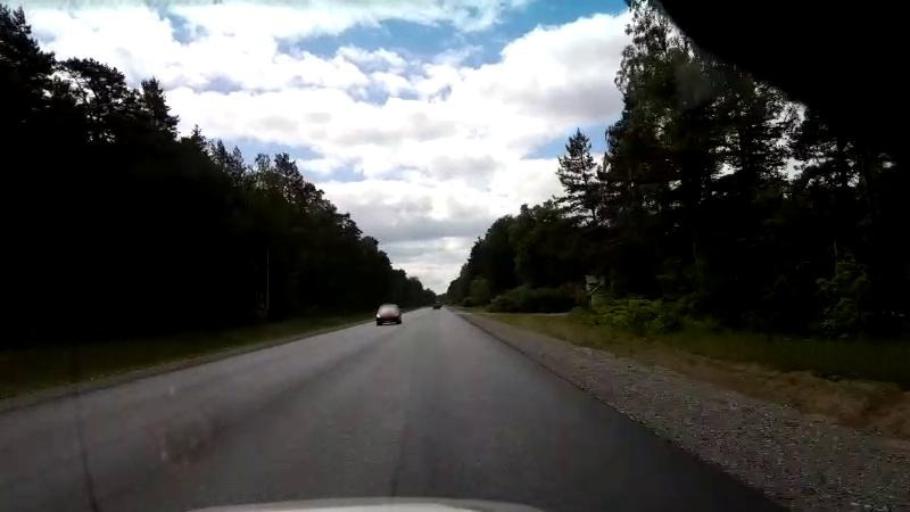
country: LV
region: Salacgrivas
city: Salacgriva
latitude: 57.8035
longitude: 24.3491
